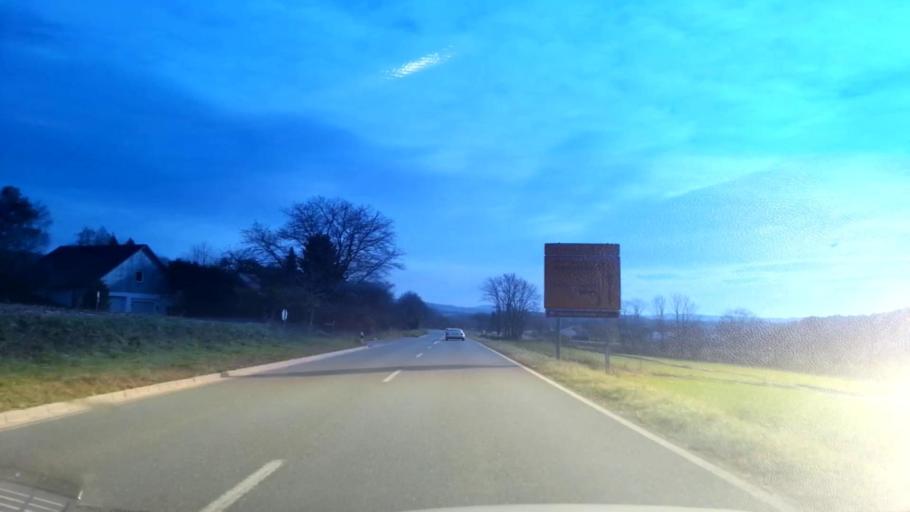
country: DE
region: Bavaria
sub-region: Upper Franconia
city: Reuth
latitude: 49.9735
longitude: 11.6806
